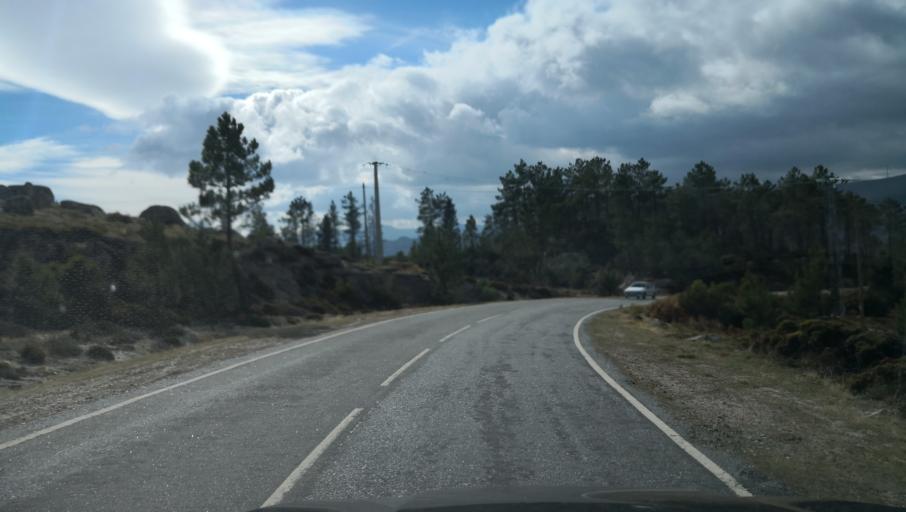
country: PT
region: Vila Real
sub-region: Vila Real
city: Vila Real
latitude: 41.3426
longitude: -7.7877
